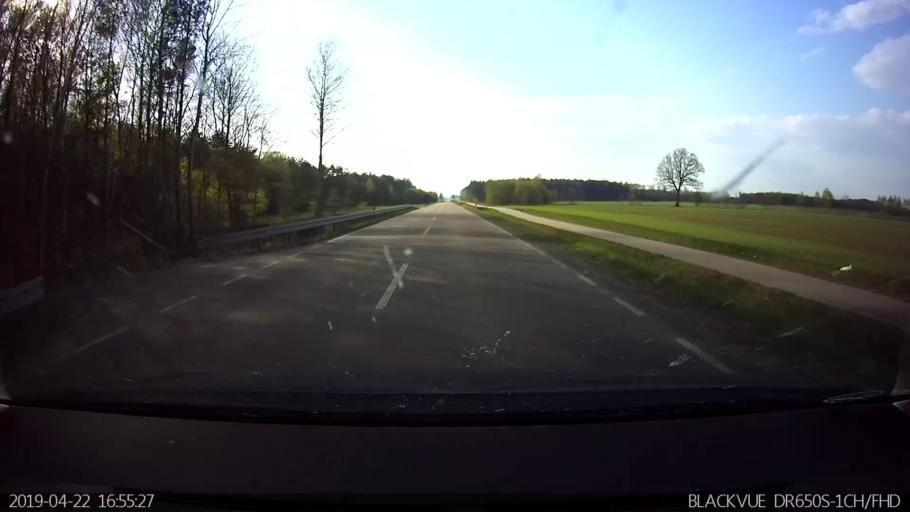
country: PL
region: Podlasie
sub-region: Powiat siemiatycki
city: Siemiatycze
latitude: 52.4755
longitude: 22.7893
